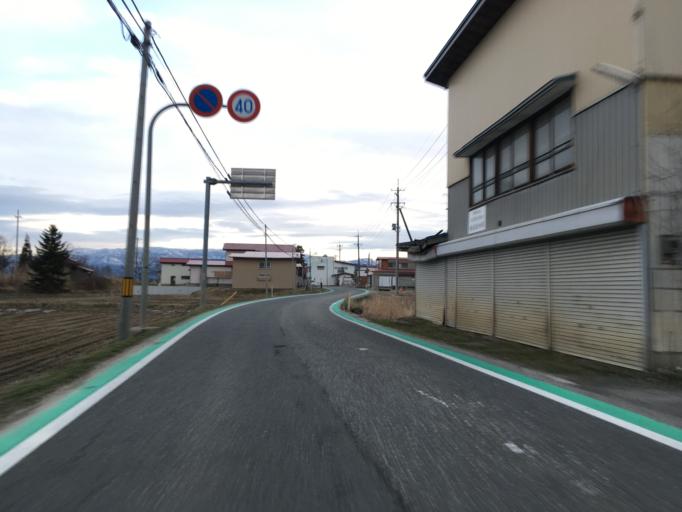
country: JP
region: Yamagata
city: Yonezawa
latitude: 37.9703
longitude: 140.0661
